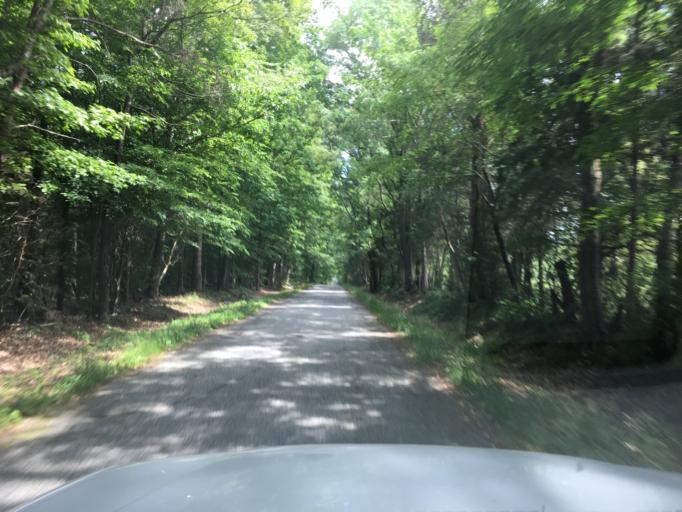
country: US
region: South Carolina
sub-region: Laurens County
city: Watts Mills
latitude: 34.5479
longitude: -81.9442
